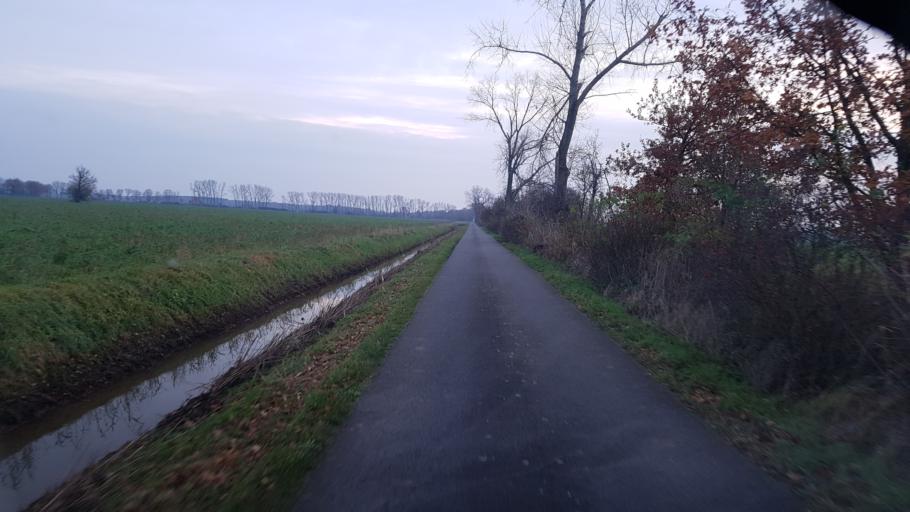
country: DE
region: Brandenburg
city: Ziltendorf
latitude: 52.2331
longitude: 14.6641
